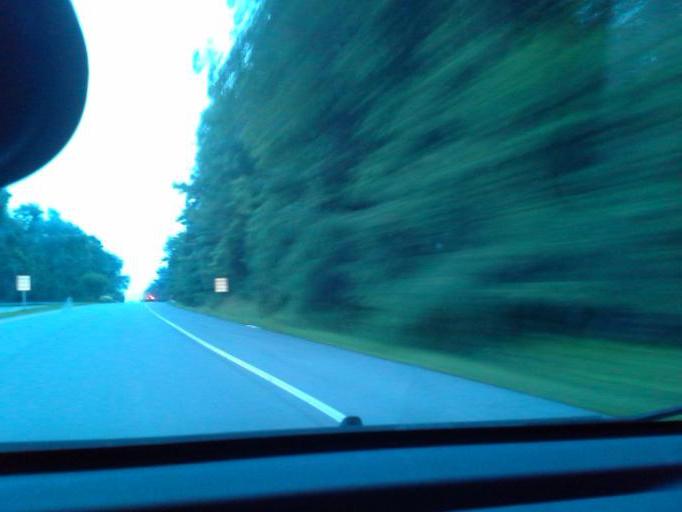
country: US
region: Maryland
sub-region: Calvert County
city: Chesapeake Beach
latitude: 38.6972
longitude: -76.5436
